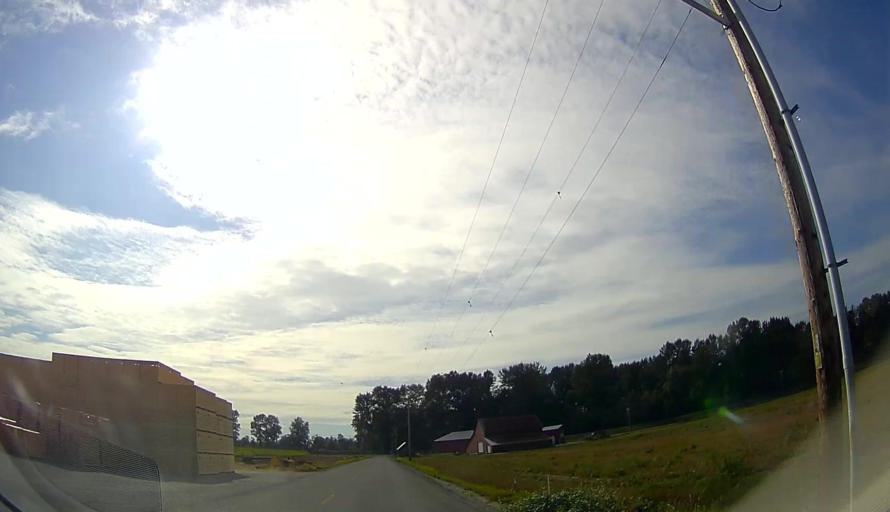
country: US
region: Washington
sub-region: Skagit County
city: Mount Vernon
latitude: 48.3704
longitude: -122.3540
